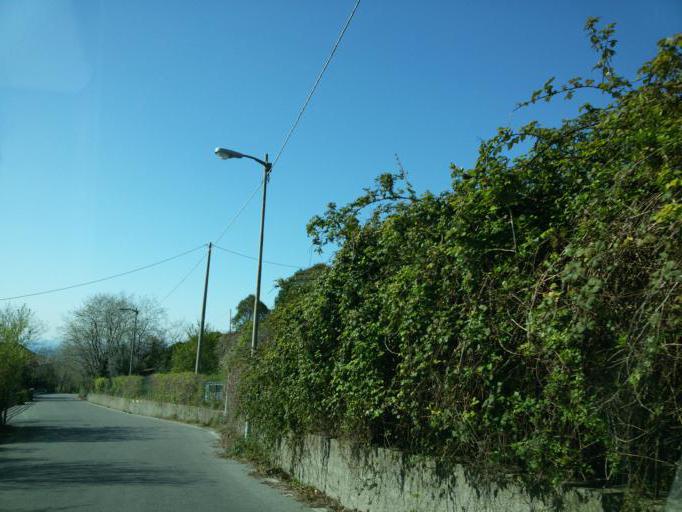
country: IT
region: Liguria
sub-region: Provincia di Genova
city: San Teodoro
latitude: 44.4238
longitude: 8.9040
